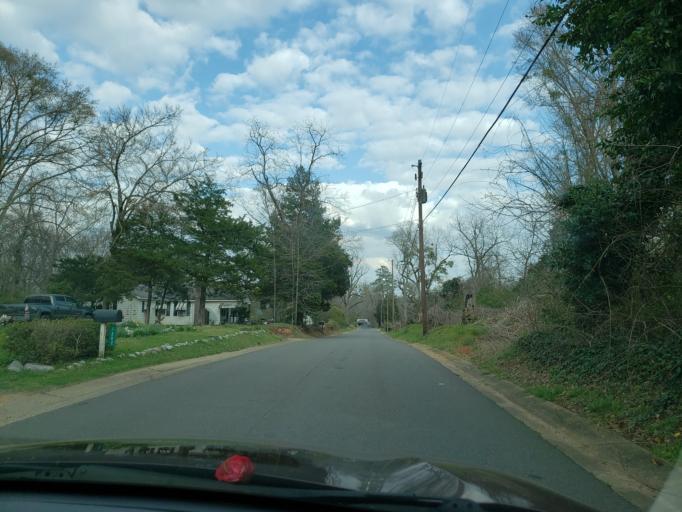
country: US
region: Alabama
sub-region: Hale County
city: Greensboro
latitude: 32.7103
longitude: -87.5946
